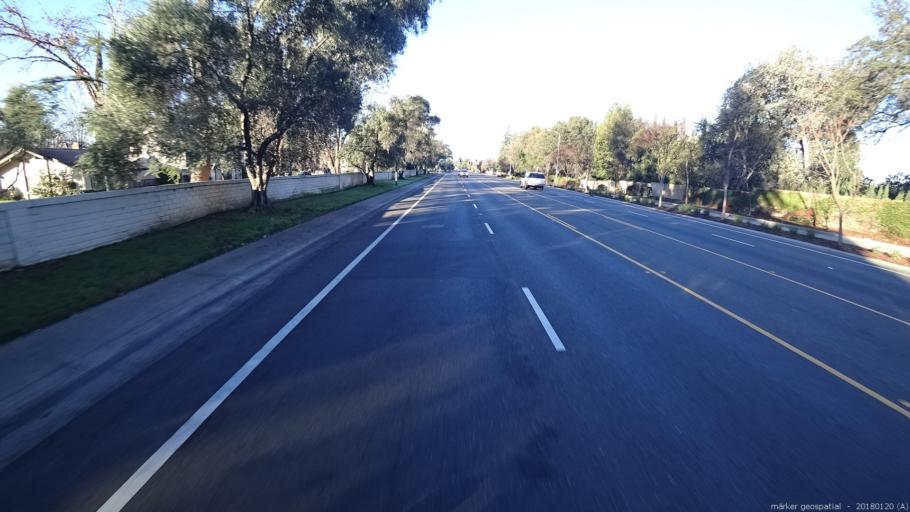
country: US
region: California
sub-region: Sacramento County
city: Fair Oaks
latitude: 38.6171
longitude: -121.2766
